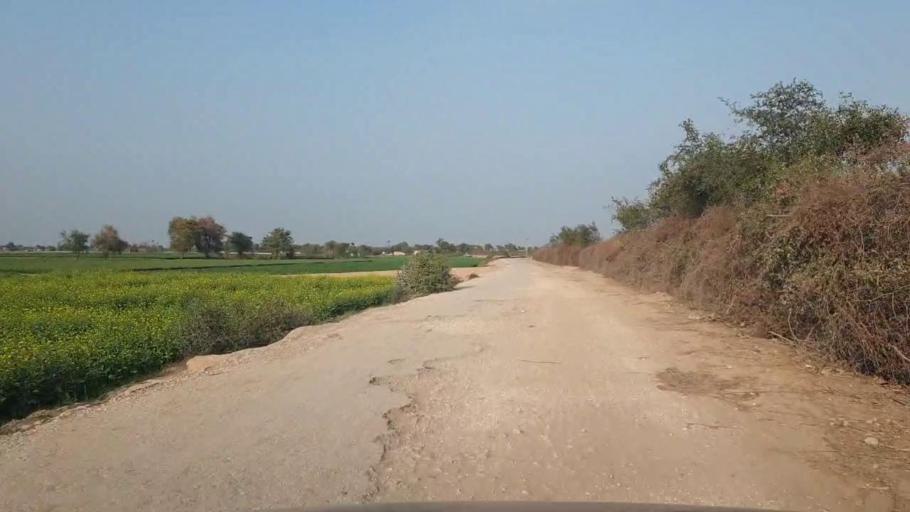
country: PK
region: Sindh
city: Bhit Shah
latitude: 25.7954
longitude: 68.4590
